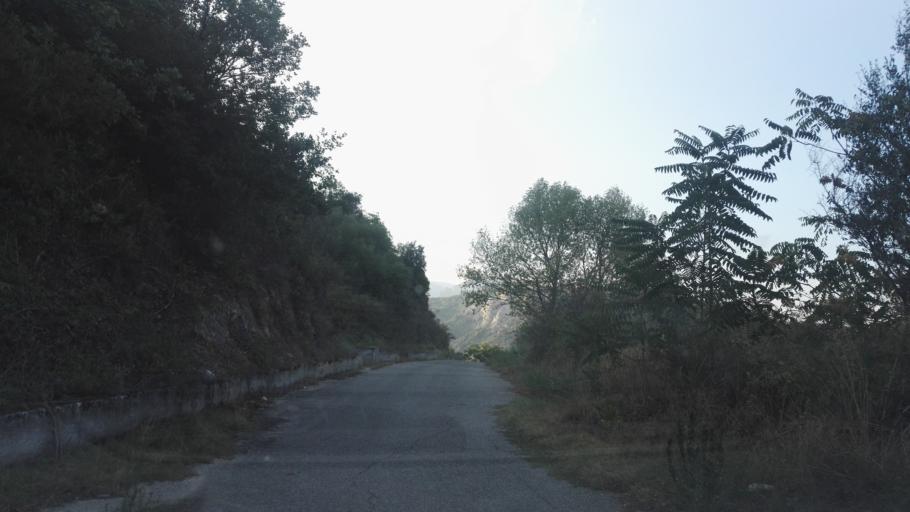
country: IT
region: Calabria
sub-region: Provincia di Reggio Calabria
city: Camini
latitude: 38.4337
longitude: 16.4803
